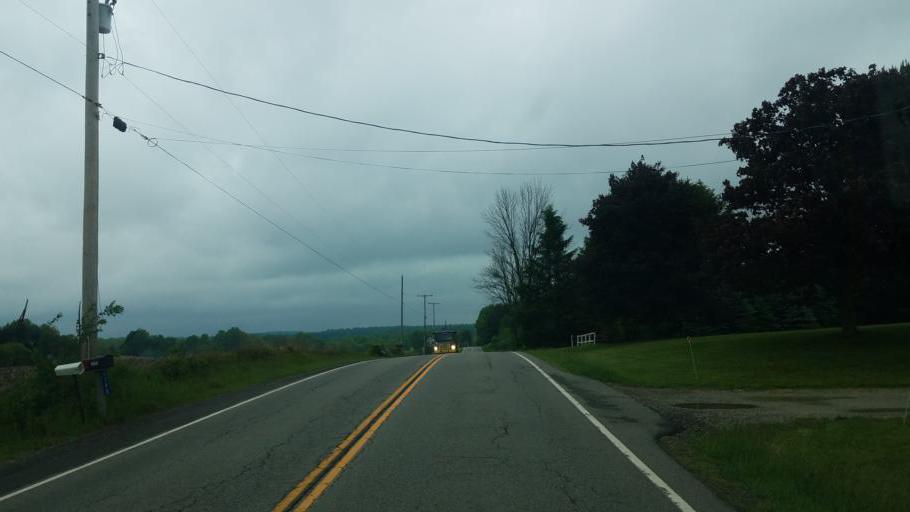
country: US
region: Ohio
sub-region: Ashland County
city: Ashland
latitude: 40.7417
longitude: -82.3173
